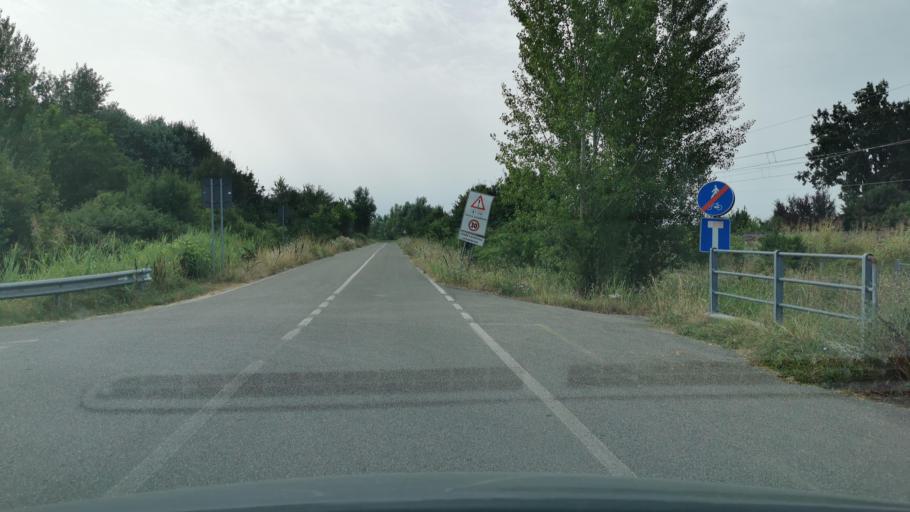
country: IT
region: Emilia-Romagna
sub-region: Provincia di Modena
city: Villanova
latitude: 44.6934
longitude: 10.9073
